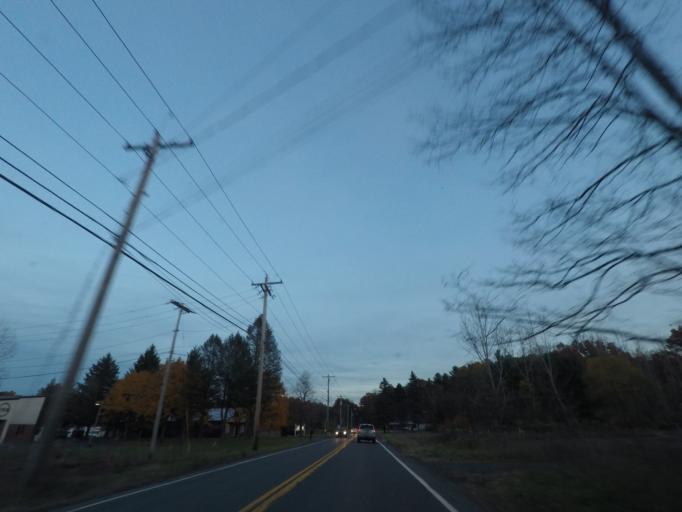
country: US
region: New York
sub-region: Albany County
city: Westmere
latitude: 42.7467
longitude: -73.9085
